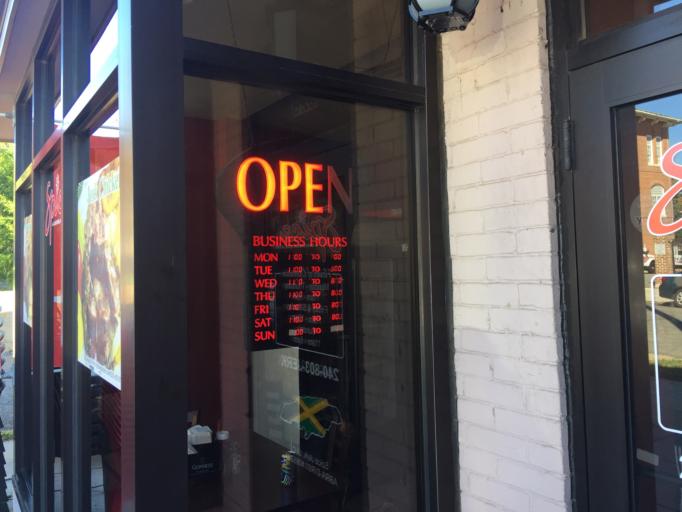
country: US
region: Maryland
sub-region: Prince George's County
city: Chillum
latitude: 38.9396
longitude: -77.0245
